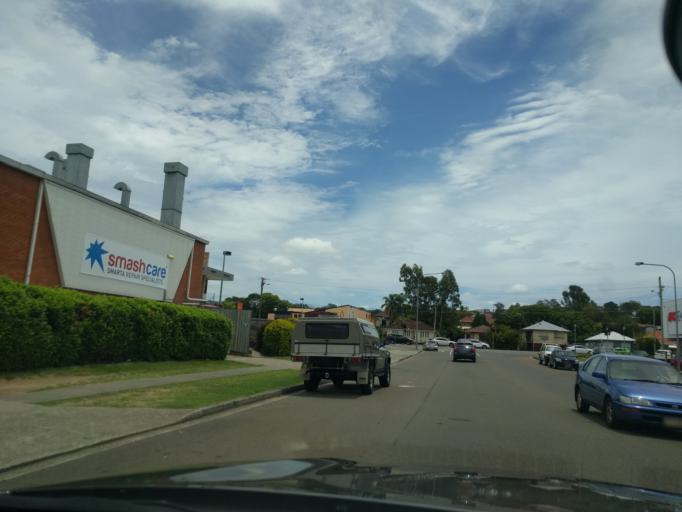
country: AU
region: Queensland
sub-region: Brisbane
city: Stafford
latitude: -27.4106
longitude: 153.0112
